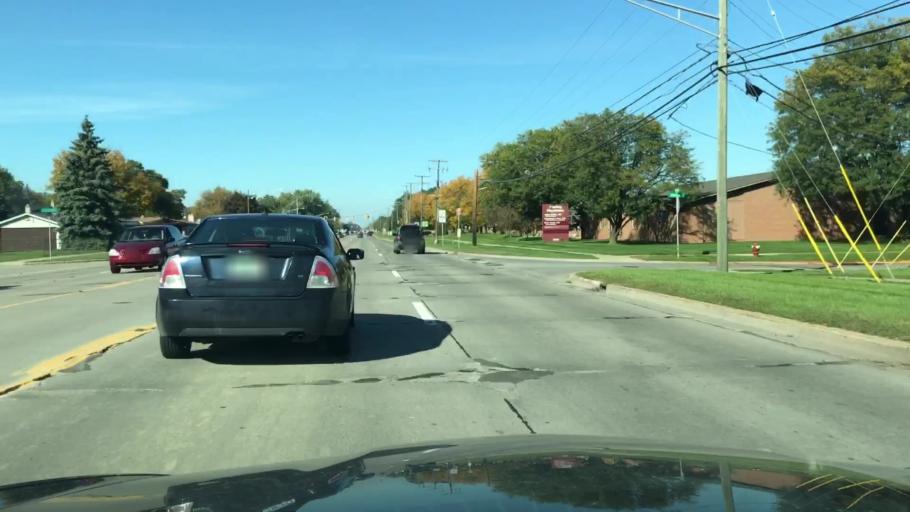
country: US
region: Michigan
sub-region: Oakland County
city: Clawson
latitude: 42.5556
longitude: -83.0884
